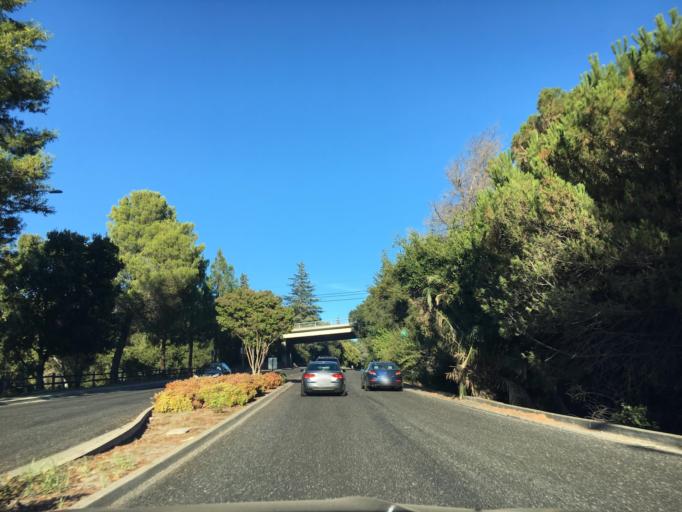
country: US
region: California
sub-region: Santa Clara County
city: Los Gatos
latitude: 37.2258
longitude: -121.9721
